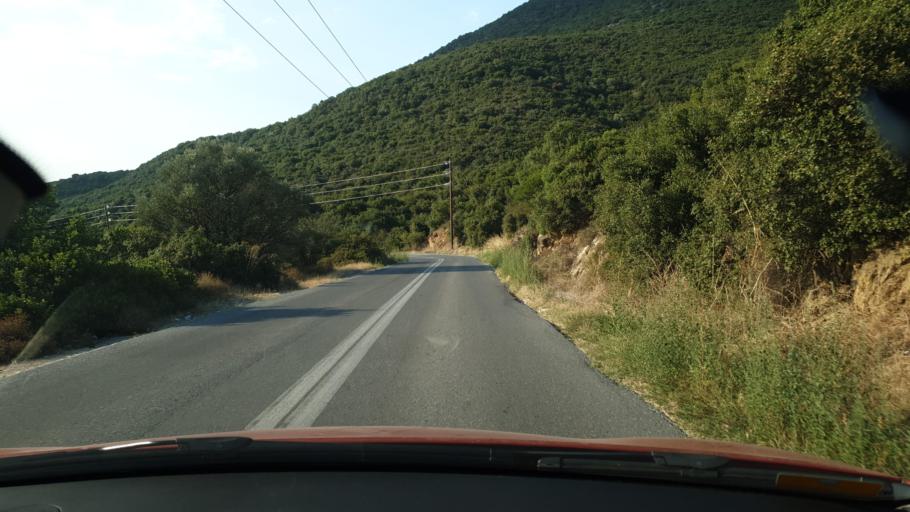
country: GR
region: Thessaly
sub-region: Nomos Magnisias
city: Pteleos
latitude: 39.0583
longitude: 22.9357
